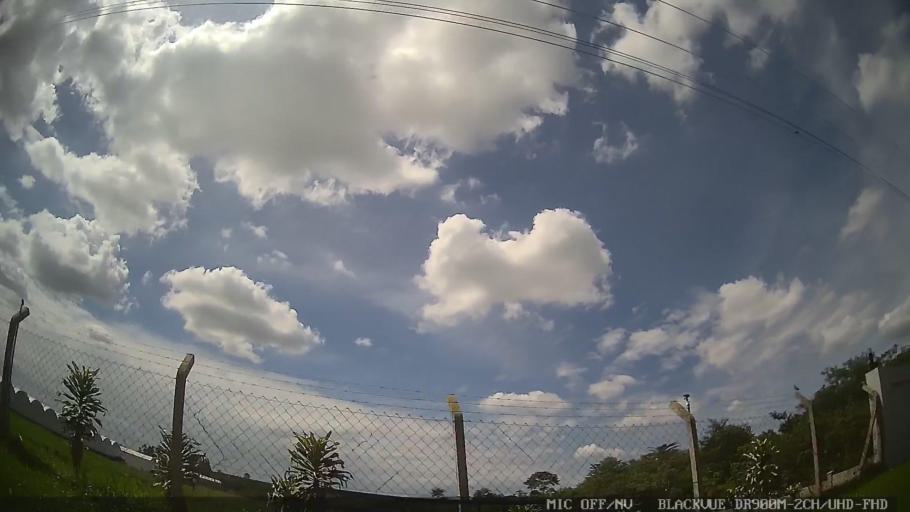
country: BR
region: Sao Paulo
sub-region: Artur Nogueira
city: Artur Nogueira
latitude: -22.5903
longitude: -47.0857
